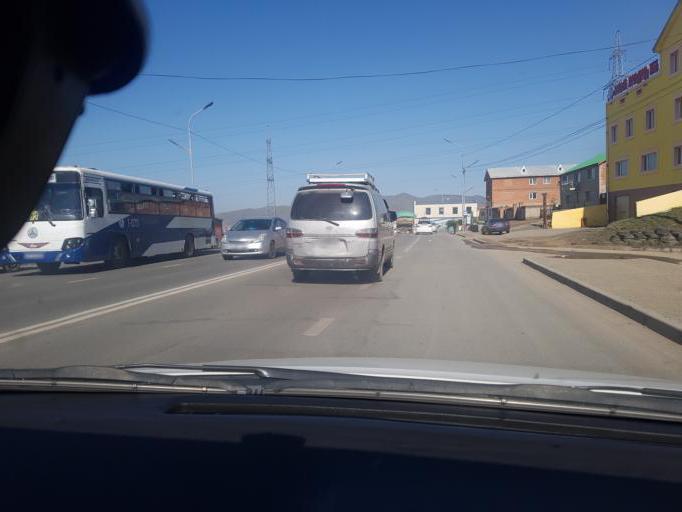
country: MN
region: Ulaanbaatar
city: Ulaanbaatar
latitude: 47.9507
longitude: 106.8601
